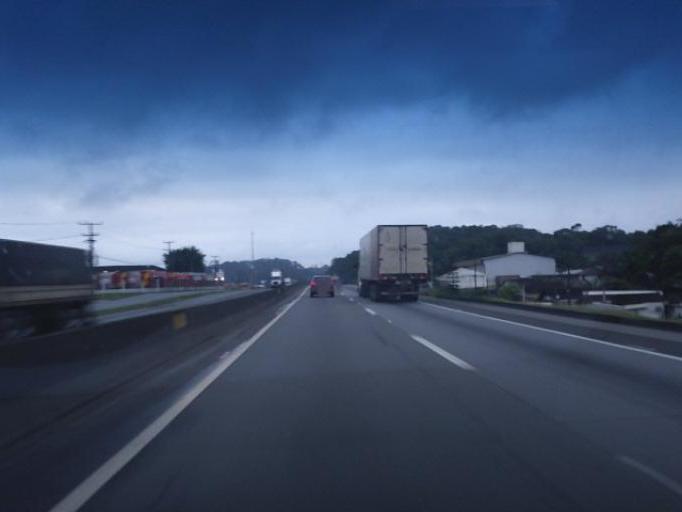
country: BR
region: Santa Catarina
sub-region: Joinville
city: Joinville
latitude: -26.2823
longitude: -48.8896
